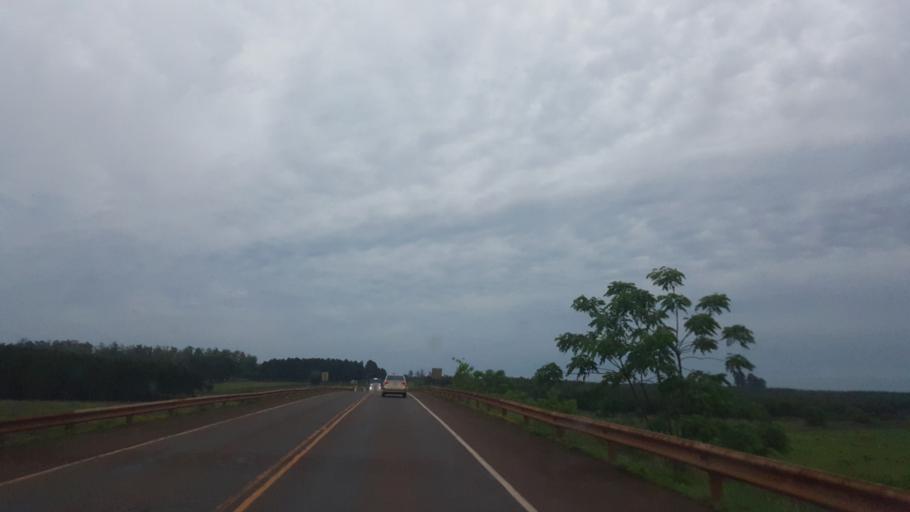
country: AR
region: Misiones
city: Garupa
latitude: -27.5989
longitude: -55.8303
